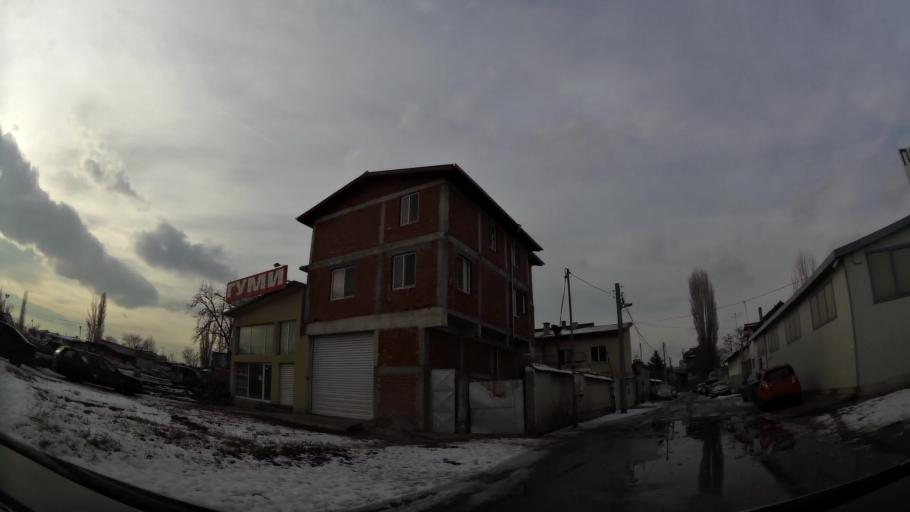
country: BG
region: Sofia-Capital
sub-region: Stolichna Obshtina
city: Sofia
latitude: 42.7116
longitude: 23.3463
